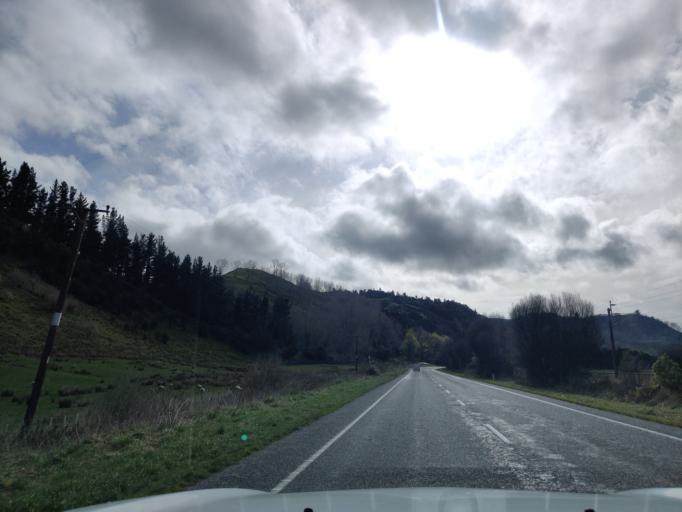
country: NZ
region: Manawatu-Wanganui
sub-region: Ruapehu District
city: Waiouru
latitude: -39.8434
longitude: 175.7408
